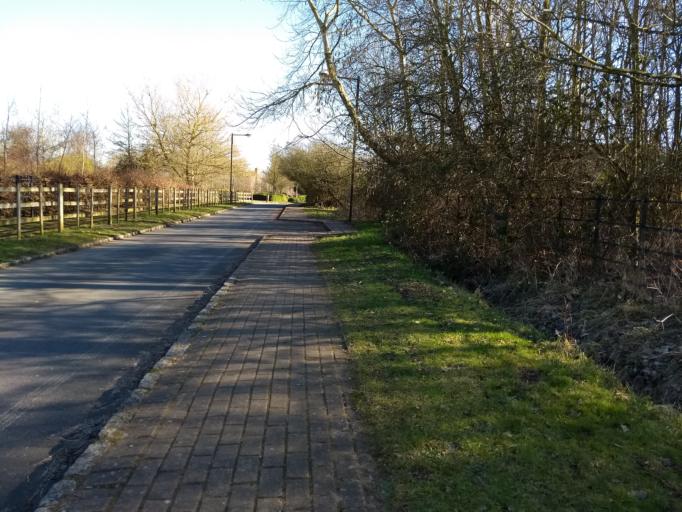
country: GB
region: England
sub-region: Milton Keynes
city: Shenley Church End
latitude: 51.9991
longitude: -0.7922
